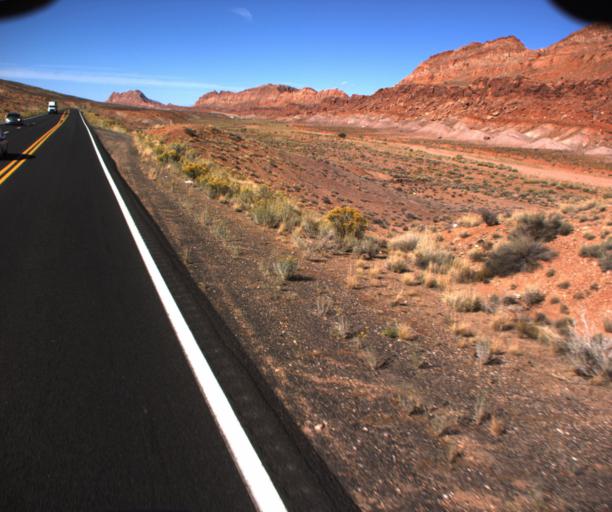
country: US
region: Arizona
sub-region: Coconino County
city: Tuba City
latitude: 36.2395
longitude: -111.4114
